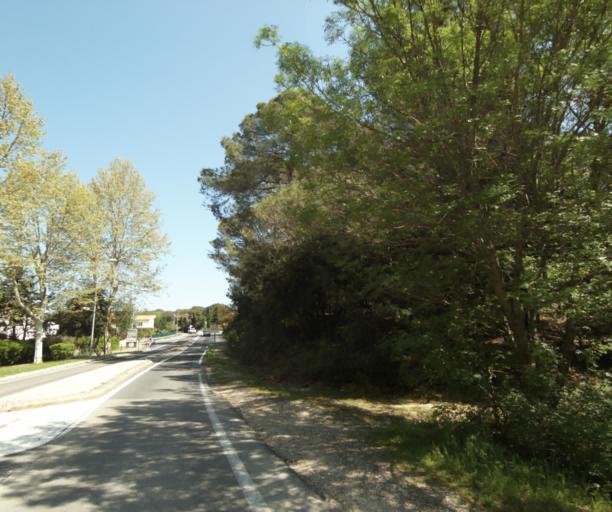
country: FR
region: Languedoc-Roussillon
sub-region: Departement de l'Herault
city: Clapiers
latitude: 43.6591
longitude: 3.8955
